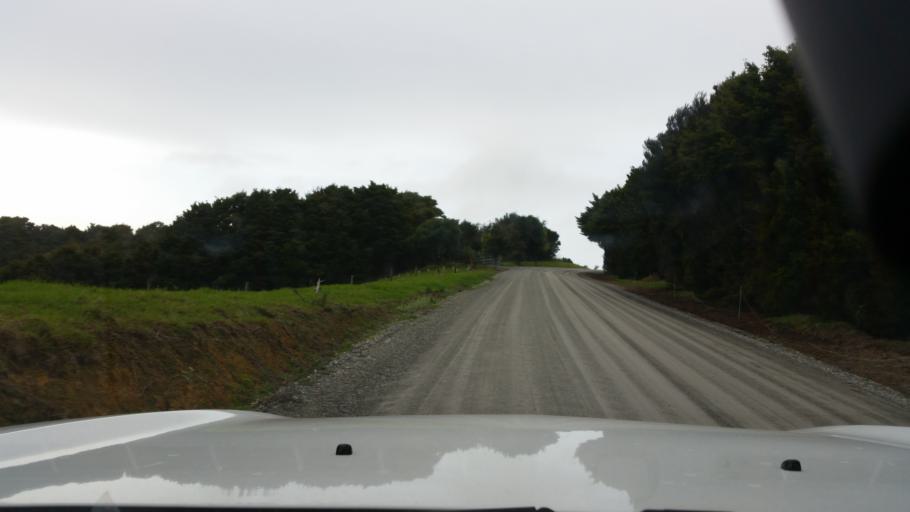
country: NZ
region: Northland
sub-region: Whangarei
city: Ngunguru
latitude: -35.7371
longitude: 174.4919
